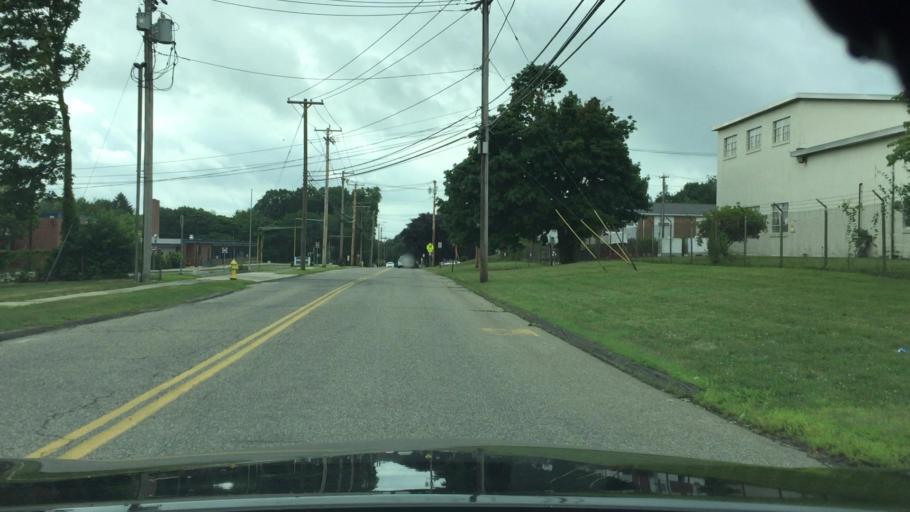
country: US
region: Connecticut
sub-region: New Haven County
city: City of Milford (balance)
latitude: 41.2123
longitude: -73.0752
